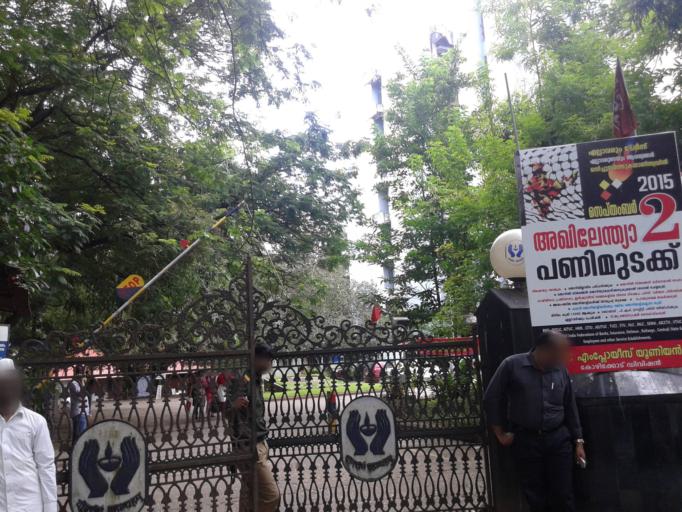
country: IN
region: Kerala
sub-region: Kozhikode
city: Kozhikode
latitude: 11.2532
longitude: 75.7820
